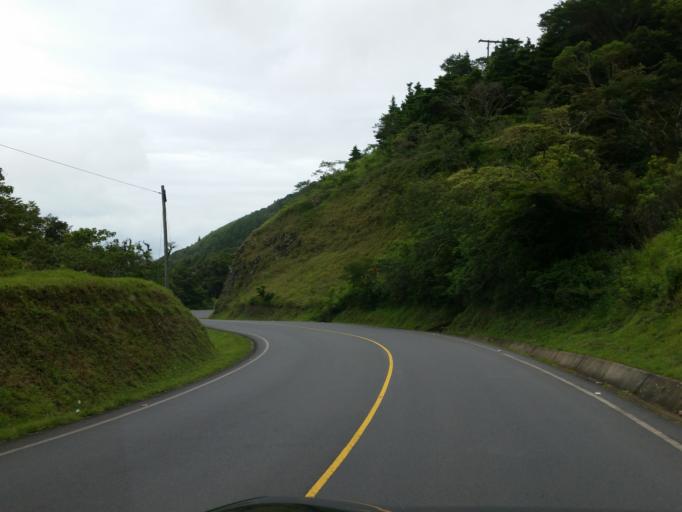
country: NI
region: Matagalpa
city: Matagalpa
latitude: 12.9908
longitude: -85.9191
